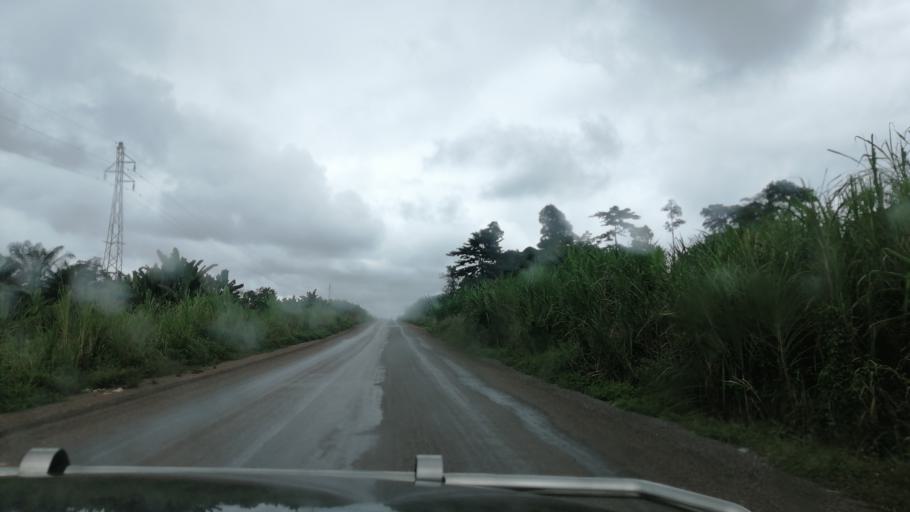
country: GH
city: Duayaw Nkwanta
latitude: 6.9050
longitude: -2.3980
